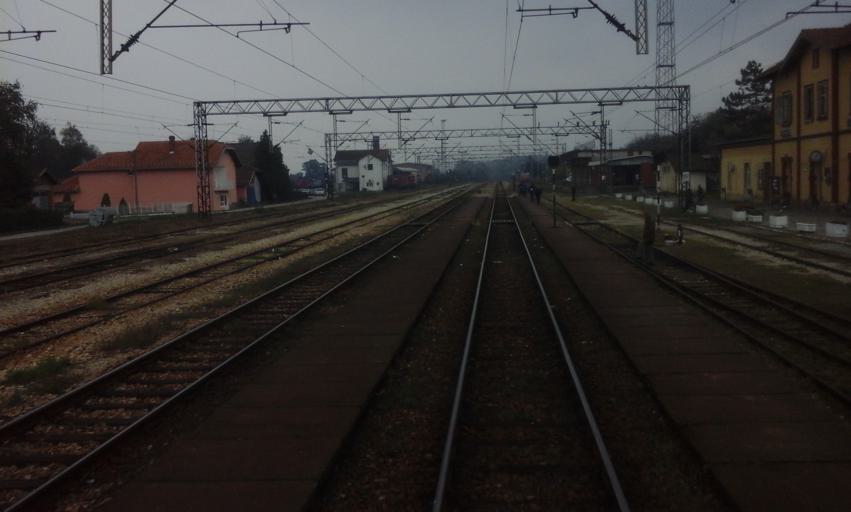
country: RS
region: Central Serbia
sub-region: Sumadijski Okrug
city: Batocina
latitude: 44.1583
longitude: 21.1019
